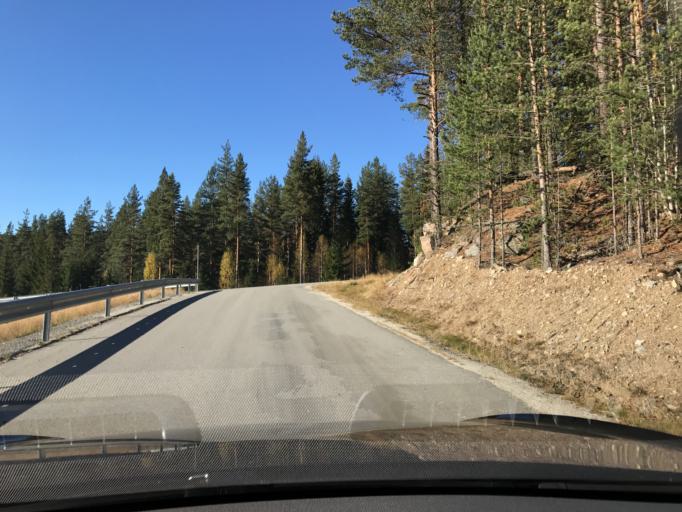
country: NO
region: Buskerud
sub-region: Krodsherad
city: Noresund
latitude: 60.2690
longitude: 9.8012
